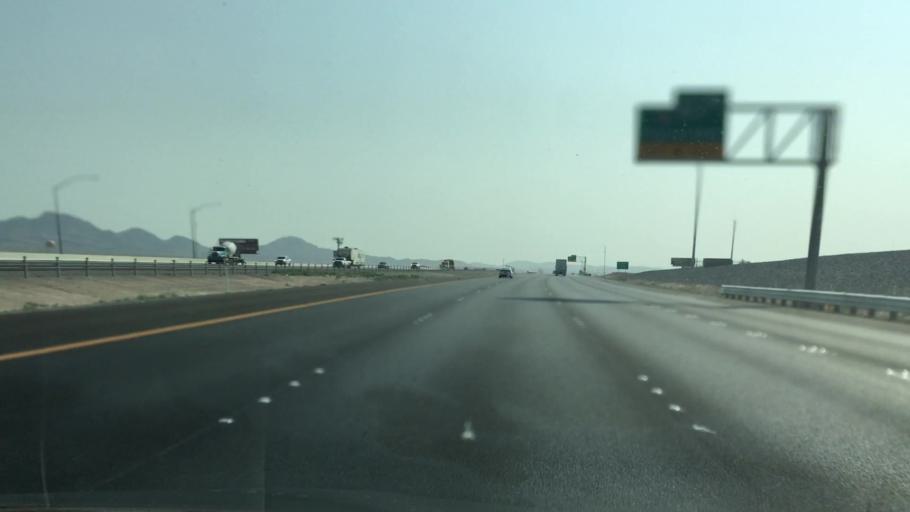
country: US
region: Nevada
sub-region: Clark County
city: Nellis Air Force Base
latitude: 36.2673
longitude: -115.0661
